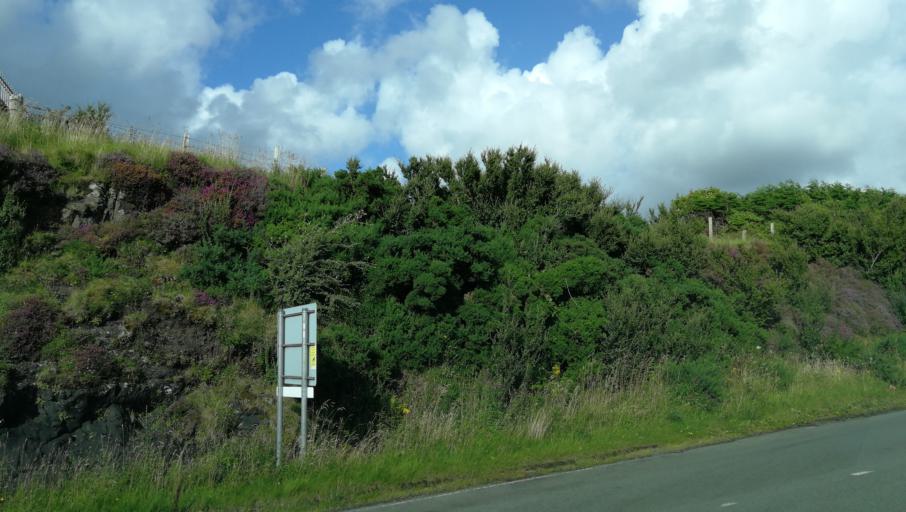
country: GB
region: Scotland
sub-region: Highland
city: Isle of Skye
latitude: 57.4367
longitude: -6.5813
